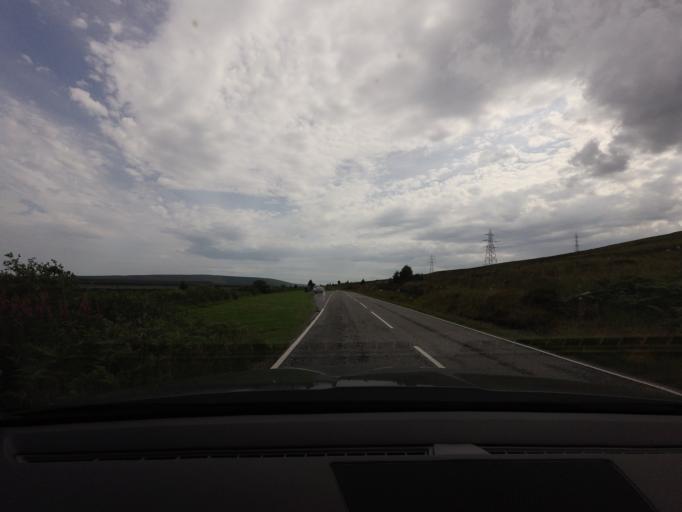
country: GB
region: Scotland
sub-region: Highland
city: Alness
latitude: 57.8202
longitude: -4.2572
